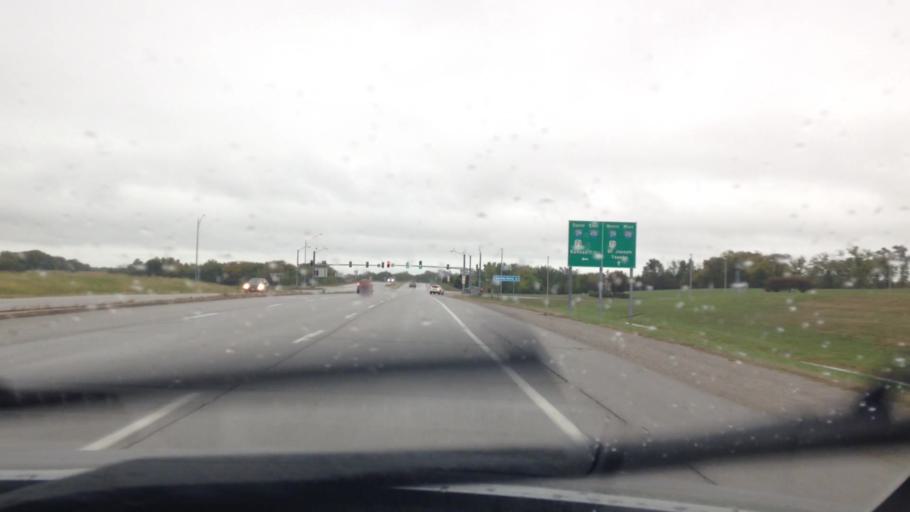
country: US
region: Missouri
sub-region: Platte County
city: Platte City
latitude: 39.3246
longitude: -94.7126
